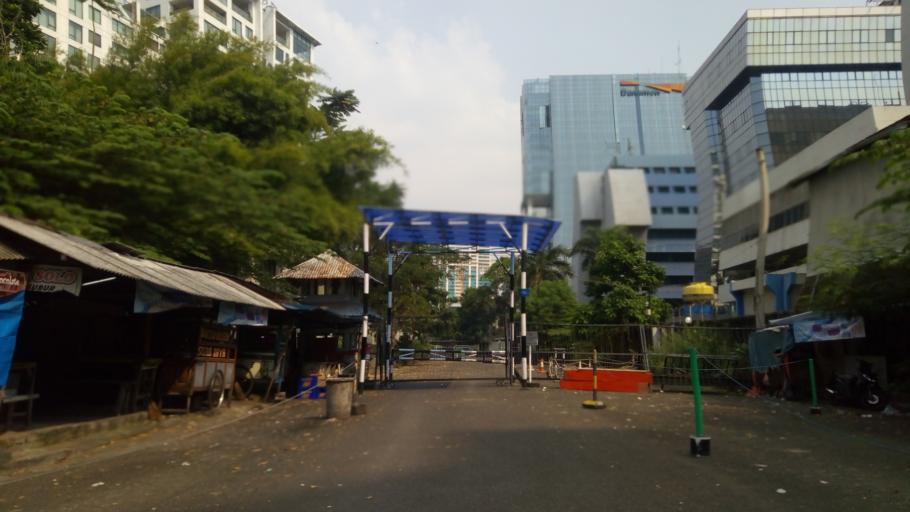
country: ID
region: Jakarta Raya
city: Jakarta
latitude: -6.2133
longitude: 106.8316
